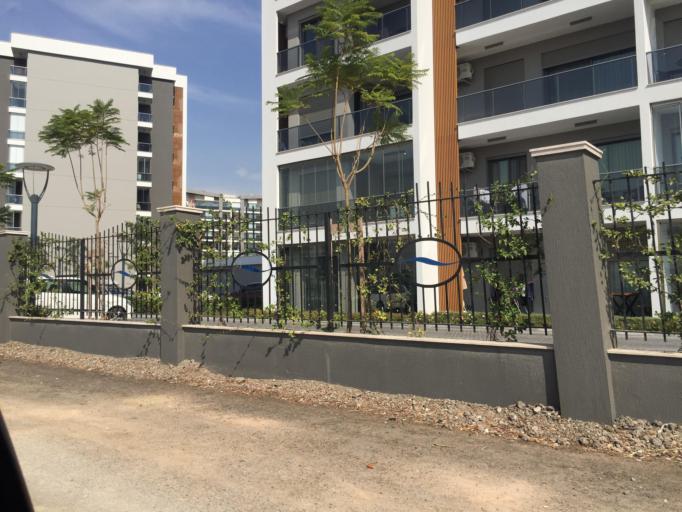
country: TR
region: Izmir
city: Karsiyaka
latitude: 38.4924
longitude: 27.0480
